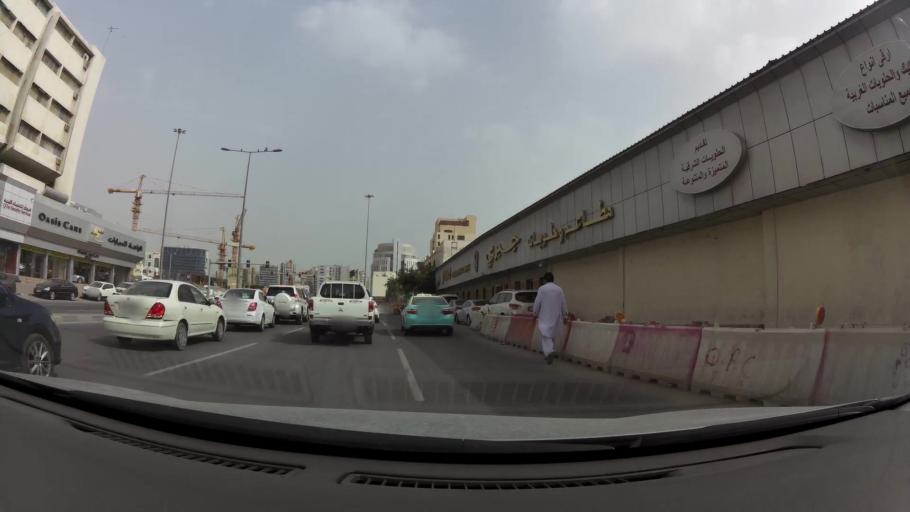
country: QA
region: Baladiyat ad Dawhah
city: Doha
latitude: 25.2819
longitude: 51.5446
